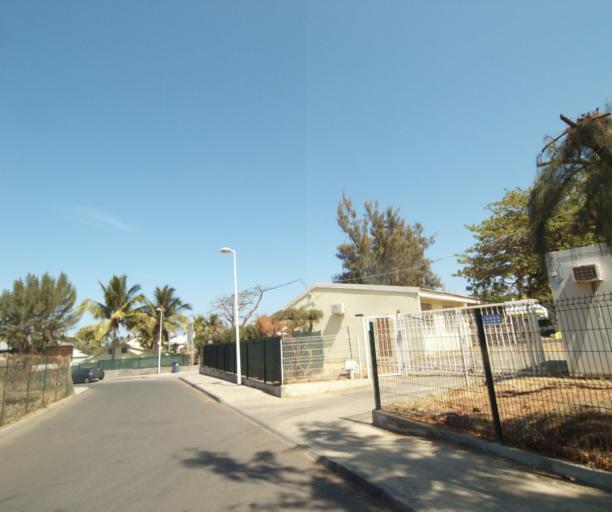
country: RE
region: Reunion
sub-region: Reunion
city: Trois-Bassins
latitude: -21.0980
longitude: 55.2439
